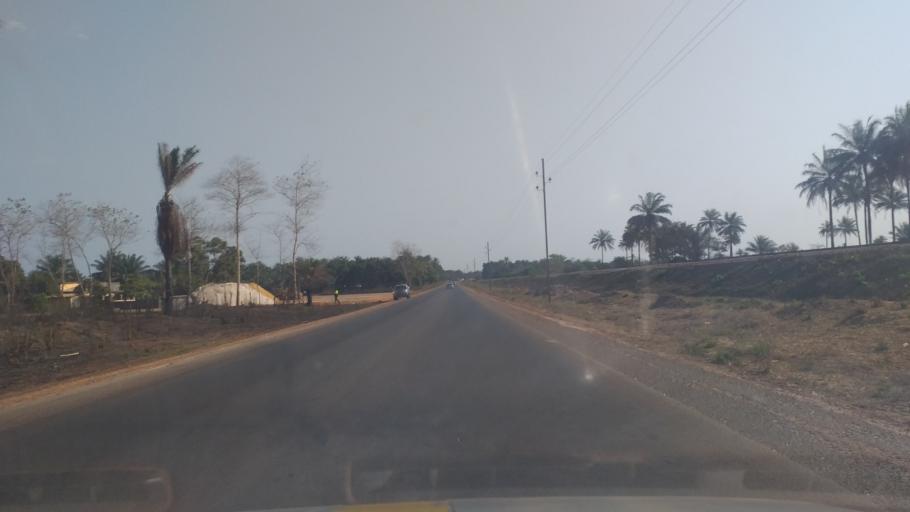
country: GN
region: Boke
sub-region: Boke Prefecture
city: Kamsar
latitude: 10.7285
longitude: -14.5181
